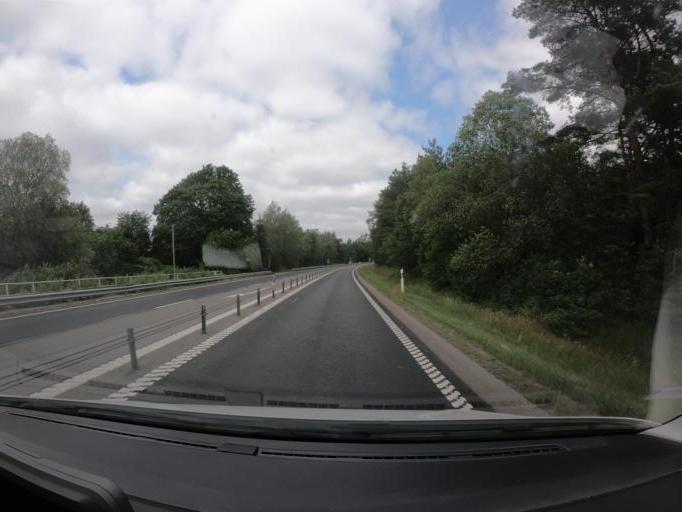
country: SE
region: Skane
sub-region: Perstorps Kommun
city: Perstorp
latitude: 56.1499
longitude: 13.5400
